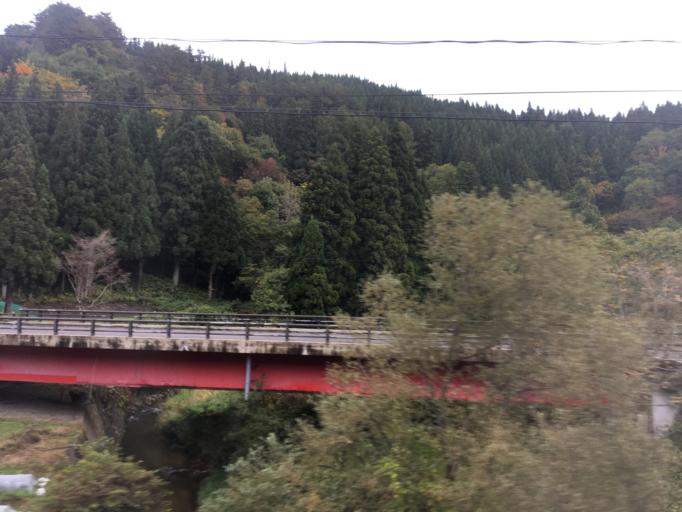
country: JP
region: Yamagata
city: Nagai
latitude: 38.0179
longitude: 139.8932
